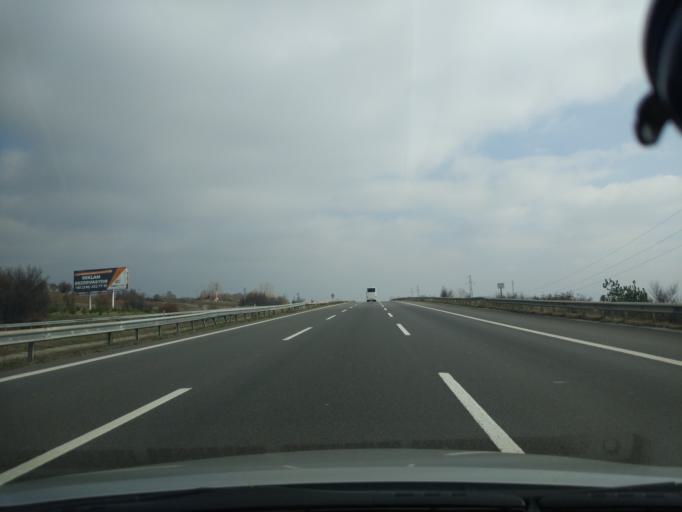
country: TR
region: Bolu
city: Bolu
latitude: 40.7631
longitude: 31.6080
